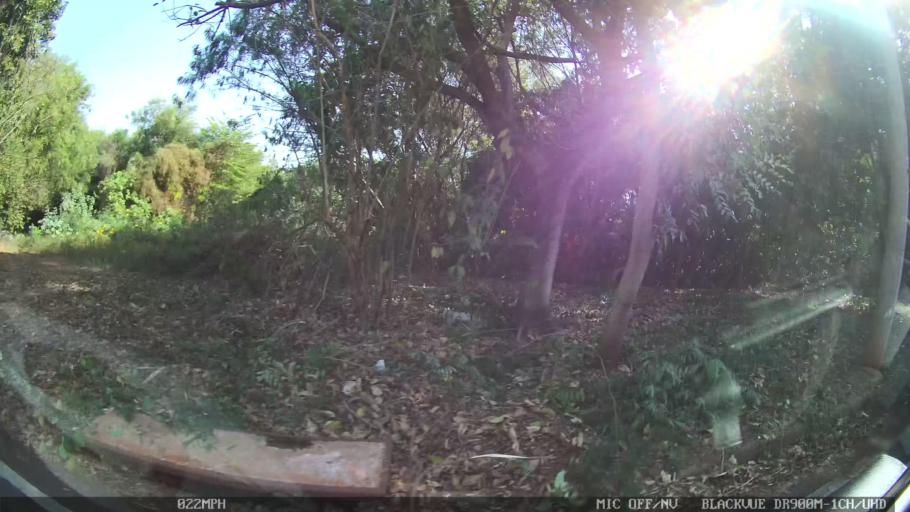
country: BR
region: Sao Paulo
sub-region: Sao Jose Do Rio Preto
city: Sao Jose do Rio Preto
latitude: -20.7963
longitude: -49.4241
